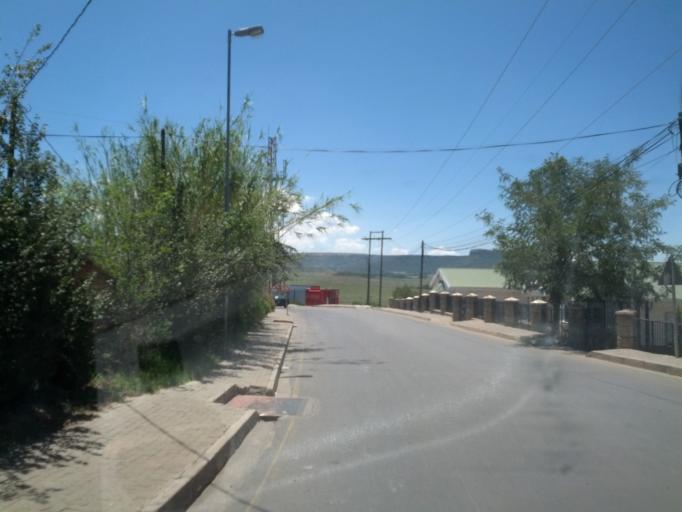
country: LS
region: Maseru
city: Maseru
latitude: -29.3059
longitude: 27.4869
